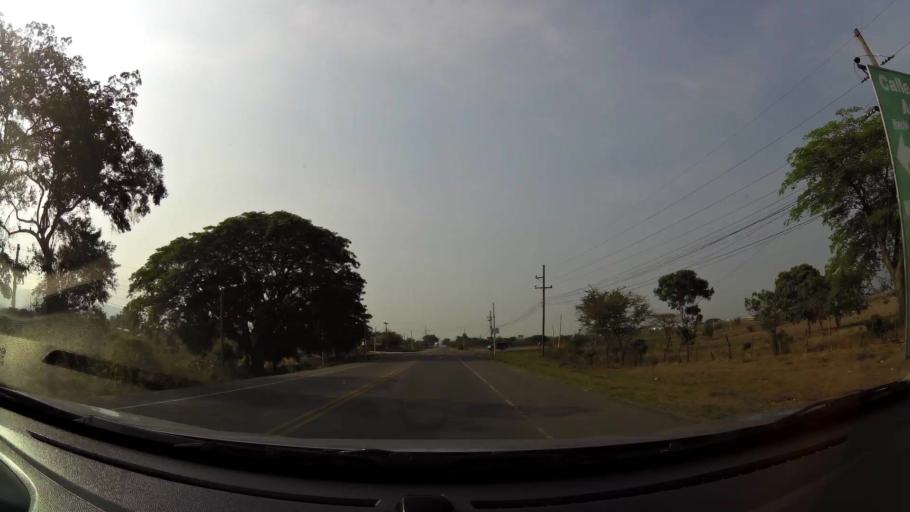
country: HN
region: Comayagua
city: Comayagua
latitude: 14.4274
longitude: -87.6298
